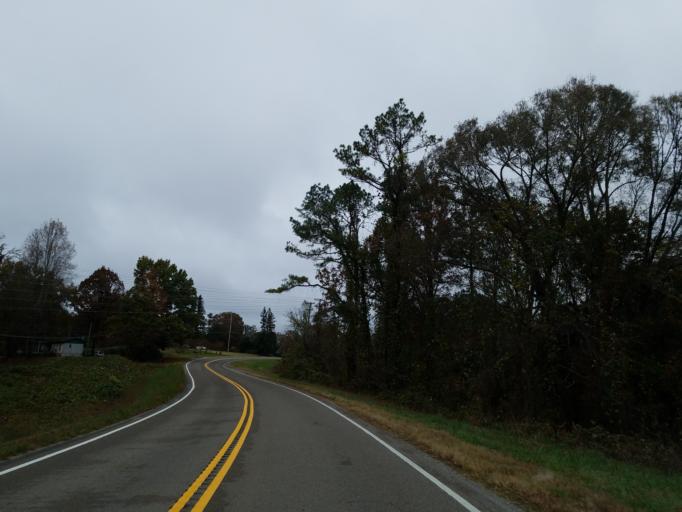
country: US
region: Georgia
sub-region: Cherokee County
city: Canton
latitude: 34.2737
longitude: -84.5806
